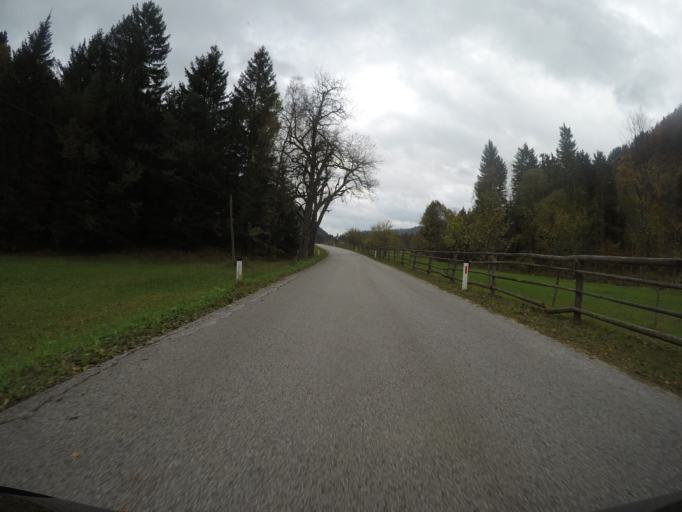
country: SI
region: Gorje
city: Zgornje Gorje
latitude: 46.3846
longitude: 14.0394
